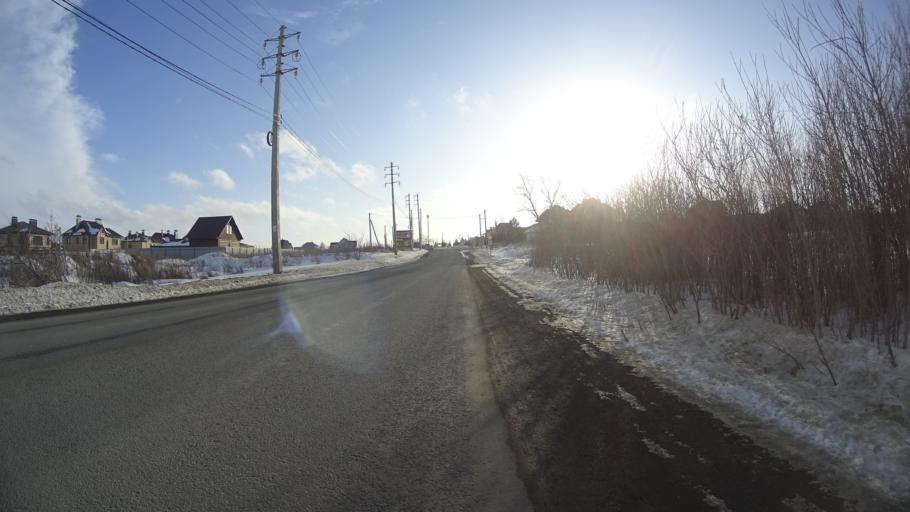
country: RU
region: Chelyabinsk
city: Sargazy
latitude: 55.1174
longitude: 61.2850
